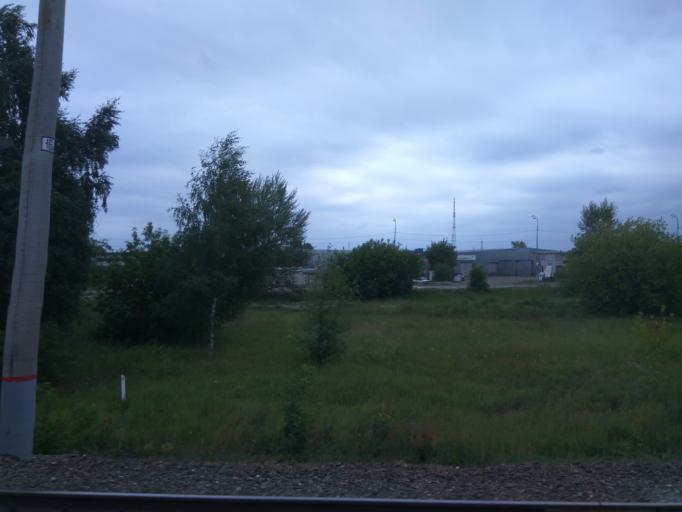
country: RU
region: Tatarstan
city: Staroye Arakchino
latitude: 55.8382
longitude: 49.0313
